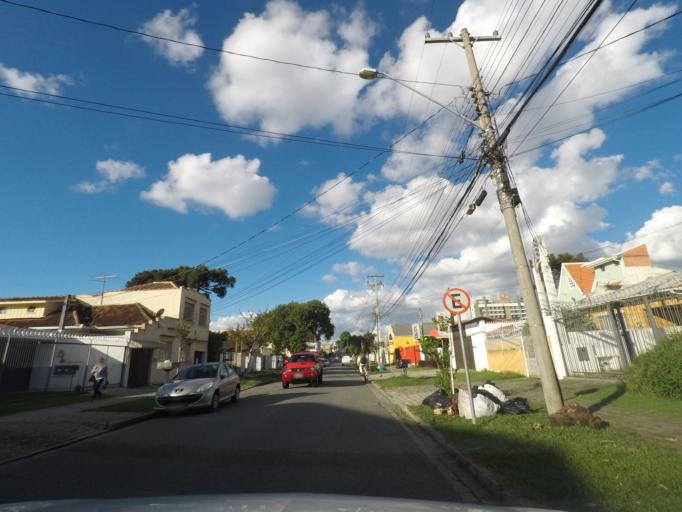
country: BR
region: Parana
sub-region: Curitiba
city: Curitiba
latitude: -25.4480
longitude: -49.2672
